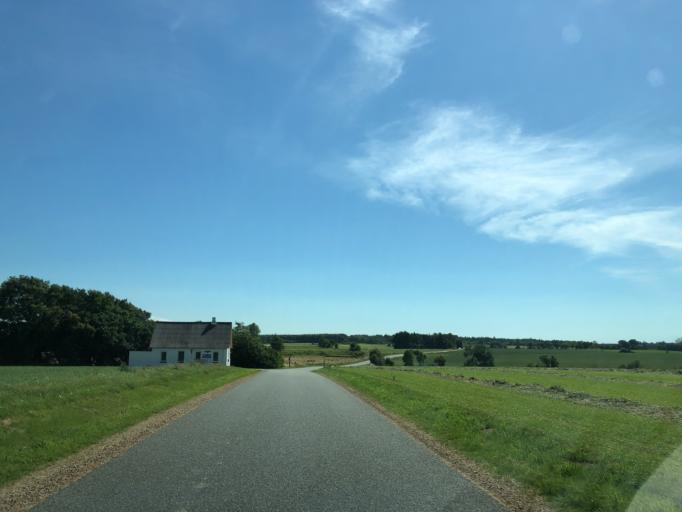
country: DK
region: Central Jutland
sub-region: Skive Kommune
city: Skive
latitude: 56.4497
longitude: 8.9770
